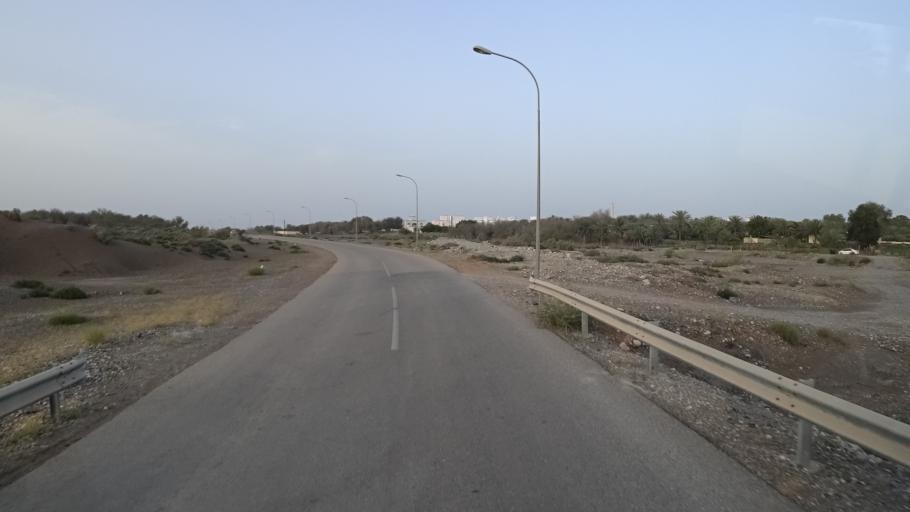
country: OM
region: Muhafazat Masqat
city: Muscat
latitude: 23.2092
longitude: 58.9727
